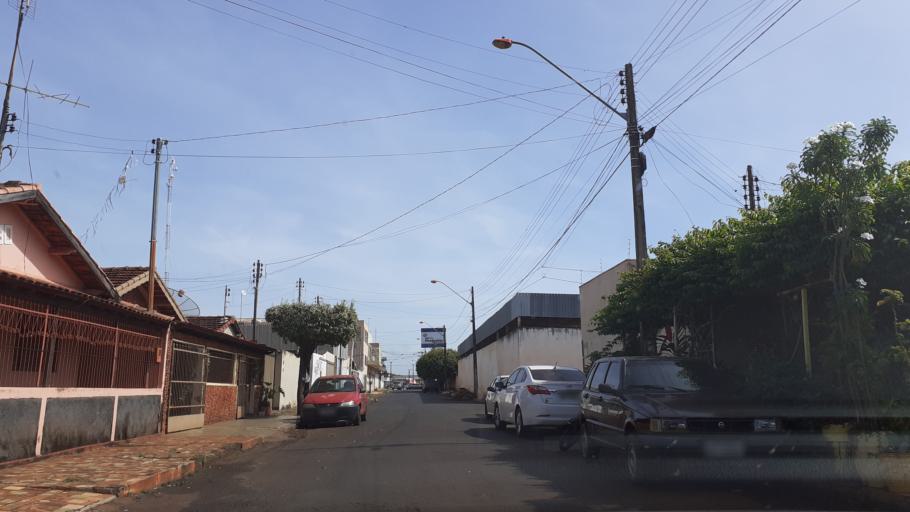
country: BR
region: Goias
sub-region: Itumbiara
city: Itumbiara
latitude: -18.4146
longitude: -49.2362
